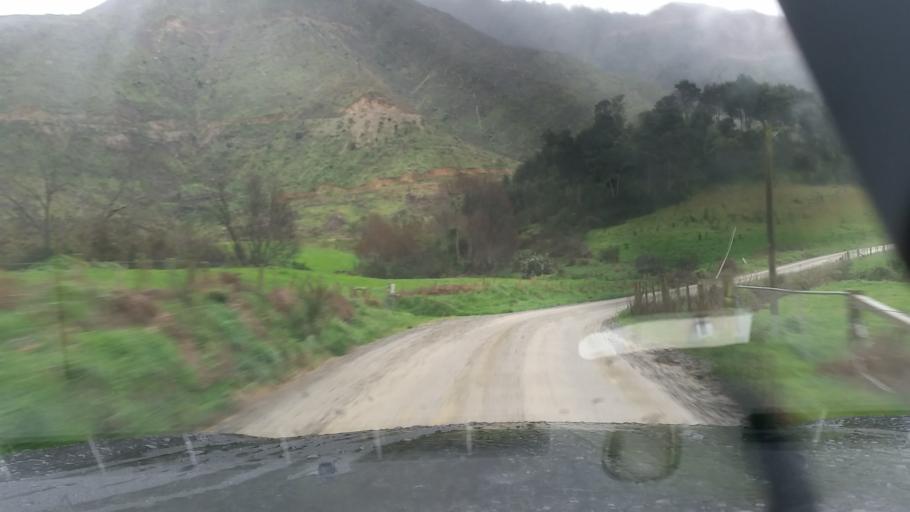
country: NZ
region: Marlborough
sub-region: Marlborough District
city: Picton
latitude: -41.3404
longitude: 173.9265
